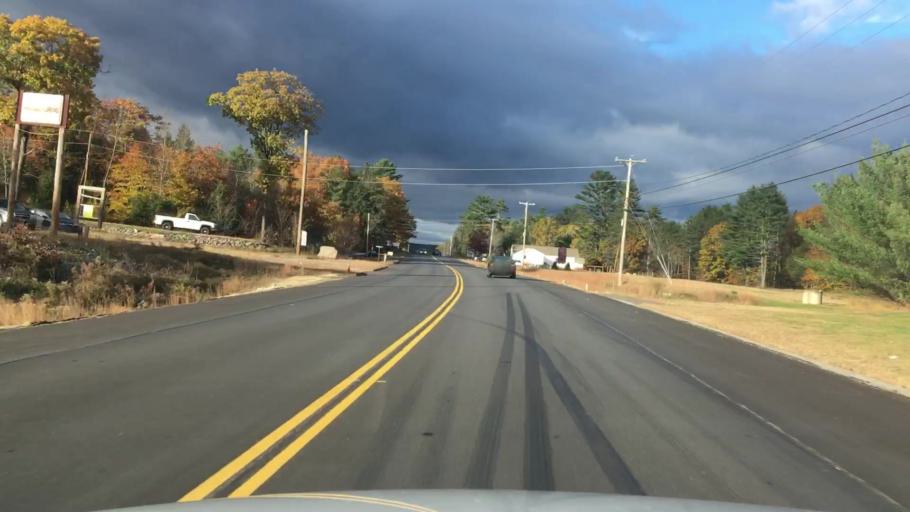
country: US
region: Maine
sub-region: Androscoggin County
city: Livermore
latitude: 44.3662
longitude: -70.2516
